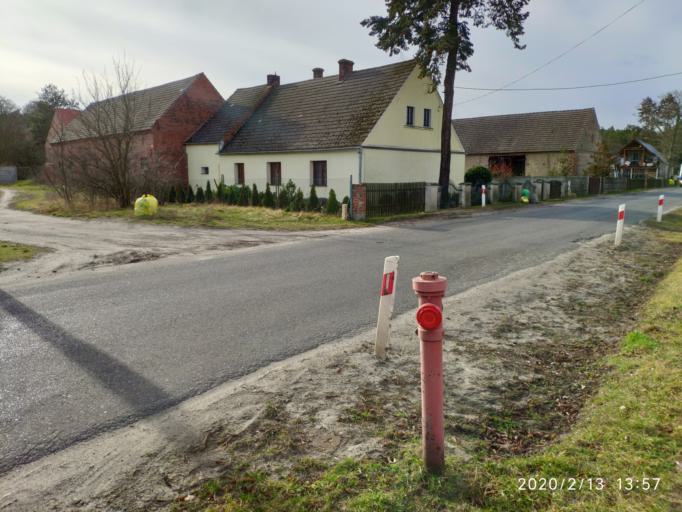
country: PL
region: Lubusz
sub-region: Zielona Gora
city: Zielona Gora
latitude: 51.9737
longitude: 15.6060
